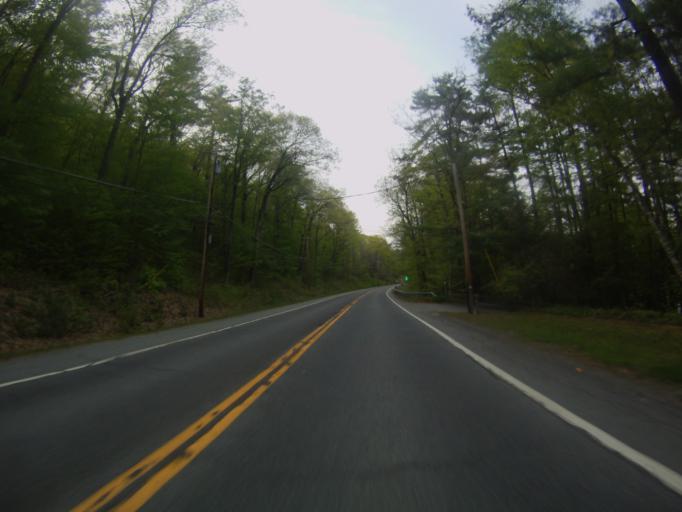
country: US
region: New York
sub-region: Essex County
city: Ticonderoga
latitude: 43.7681
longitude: -73.4902
